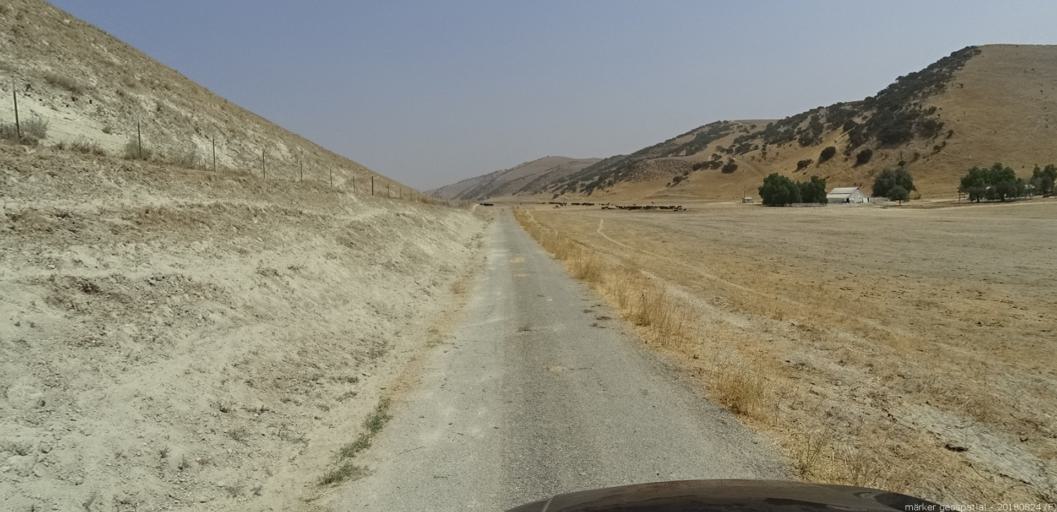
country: US
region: California
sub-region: Monterey County
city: King City
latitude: 36.2005
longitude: -120.9445
